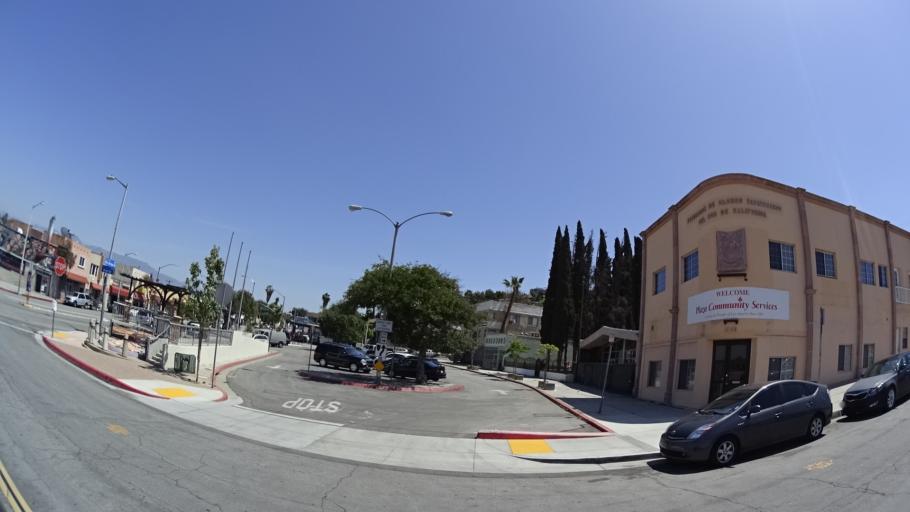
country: US
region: California
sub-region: Los Angeles County
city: Belvedere
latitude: 34.0554
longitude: -118.1777
